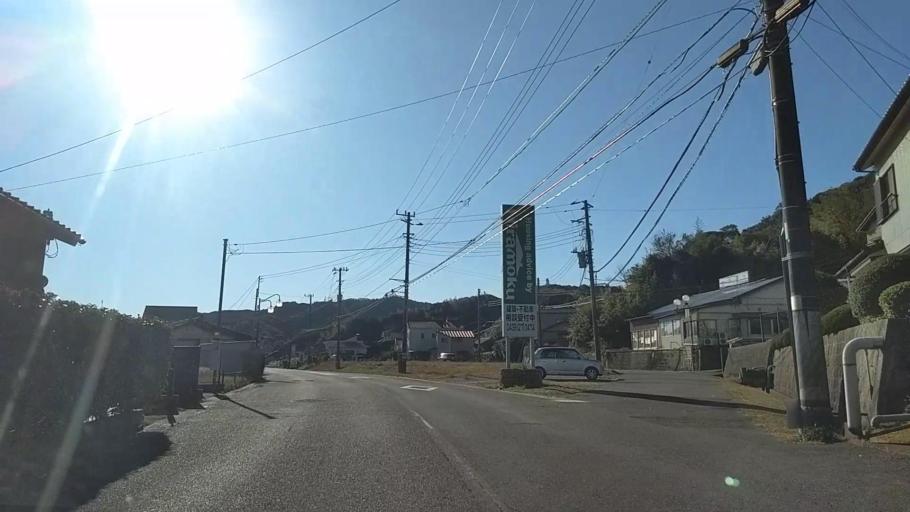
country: JP
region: Chiba
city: Futtsu
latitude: 35.2756
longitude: 139.8618
